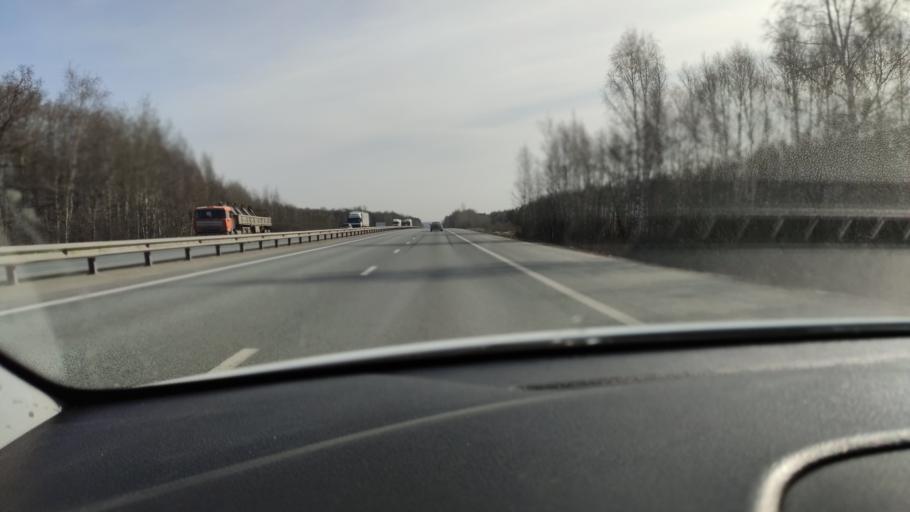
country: RU
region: Tatarstan
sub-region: Gorod Kazan'
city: Kazan
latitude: 55.9104
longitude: 49.0689
